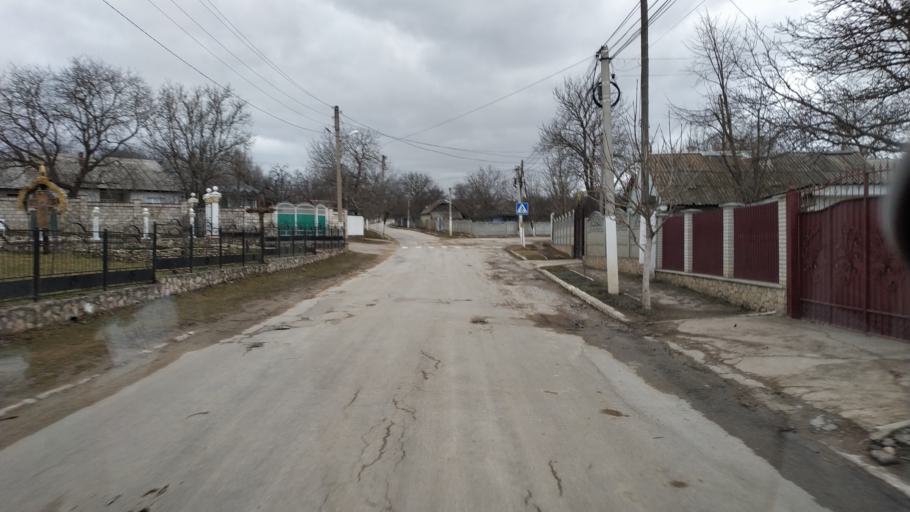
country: MD
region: Calarasi
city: Calarasi
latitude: 47.2582
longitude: 28.1390
